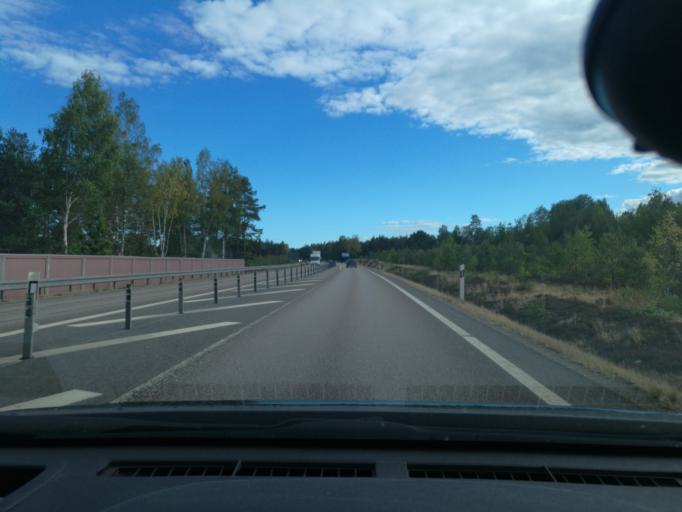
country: SE
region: Kalmar
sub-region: Oskarshamns Kommun
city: Oskarshamn
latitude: 57.3971
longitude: 16.4785
